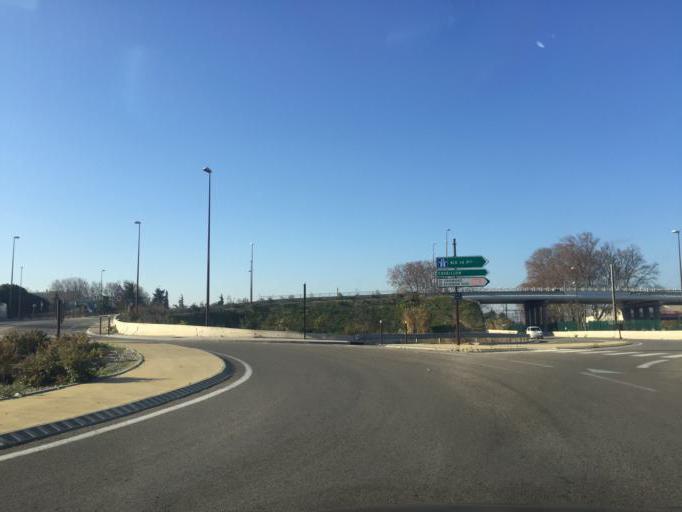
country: FR
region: Provence-Alpes-Cote d'Azur
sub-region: Departement du Vaucluse
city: Montfavet
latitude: 43.9325
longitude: 4.8487
